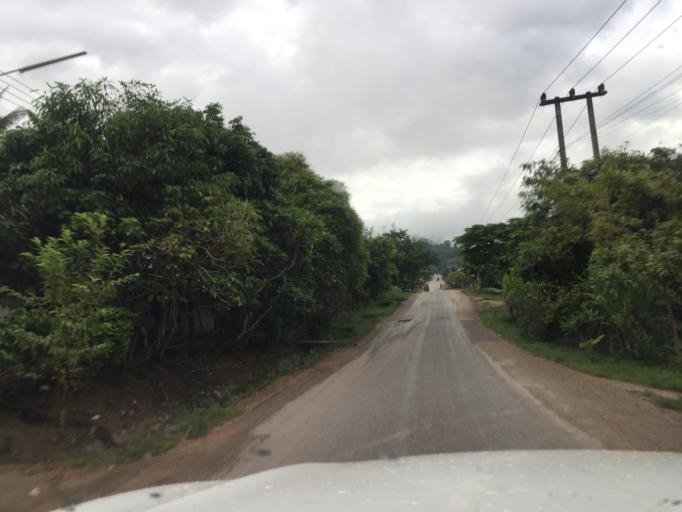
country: LA
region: Oudomxai
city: Muang La
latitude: 20.8654
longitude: 102.1165
